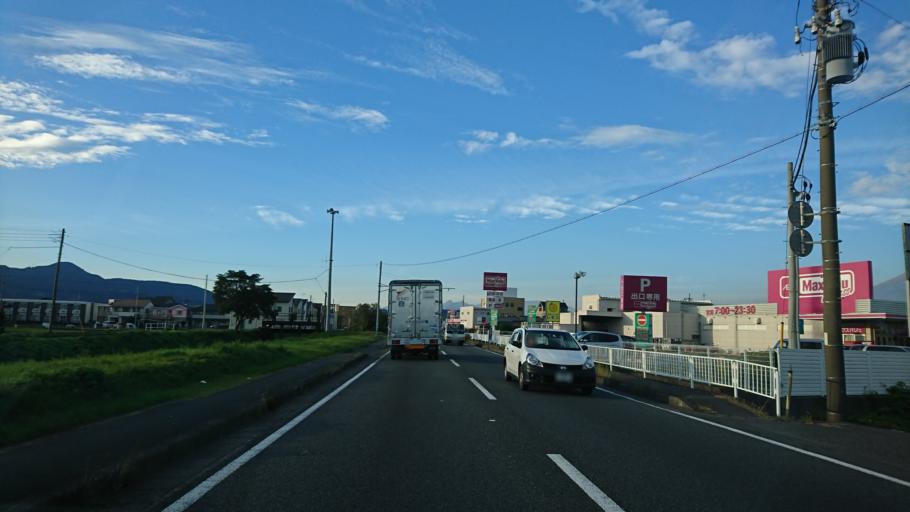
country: JP
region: Shizuoka
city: Fuji
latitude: 35.1428
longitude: 138.6480
